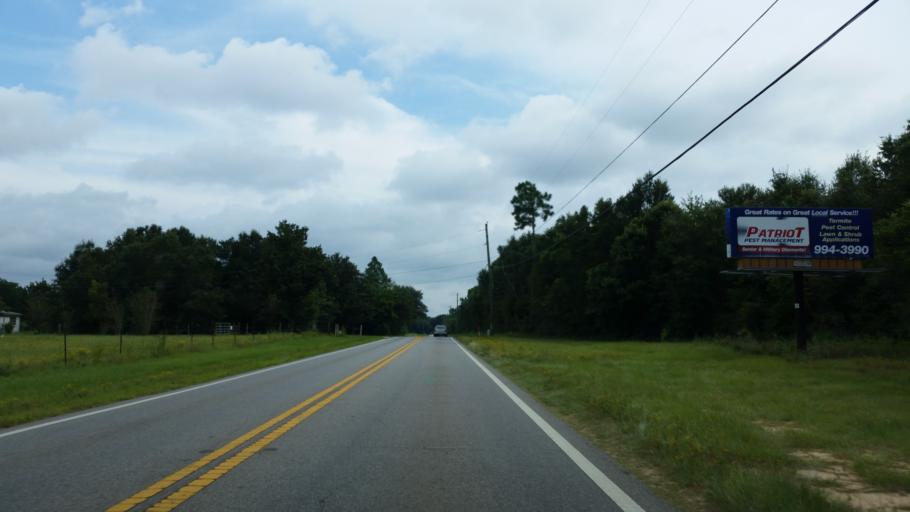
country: US
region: Florida
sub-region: Santa Rosa County
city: Wallace
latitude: 30.6457
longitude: -87.1477
